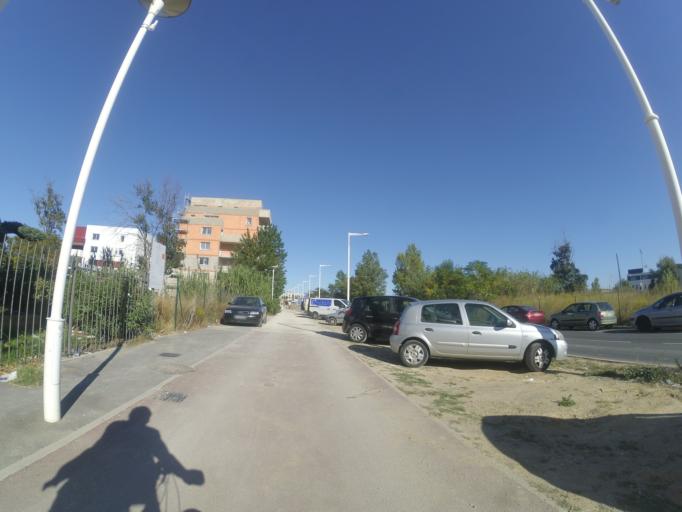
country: FR
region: Languedoc-Roussillon
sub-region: Departement des Pyrenees-Orientales
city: Perpignan
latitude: 42.6905
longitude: 2.8737
